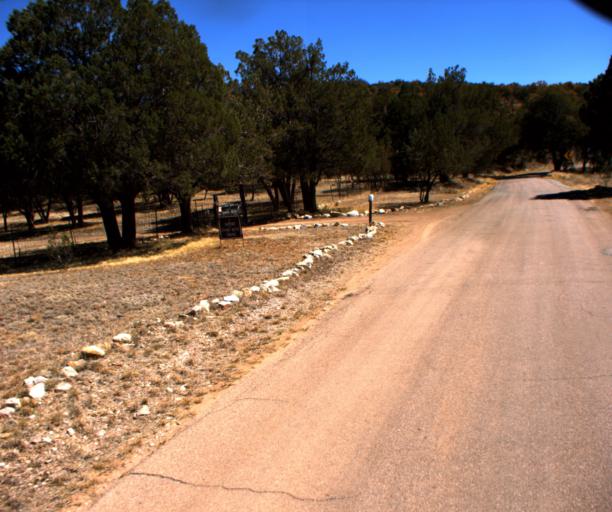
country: US
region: Arizona
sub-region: Cochise County
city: Sierra Vista
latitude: 31.4326
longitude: -110.4379
